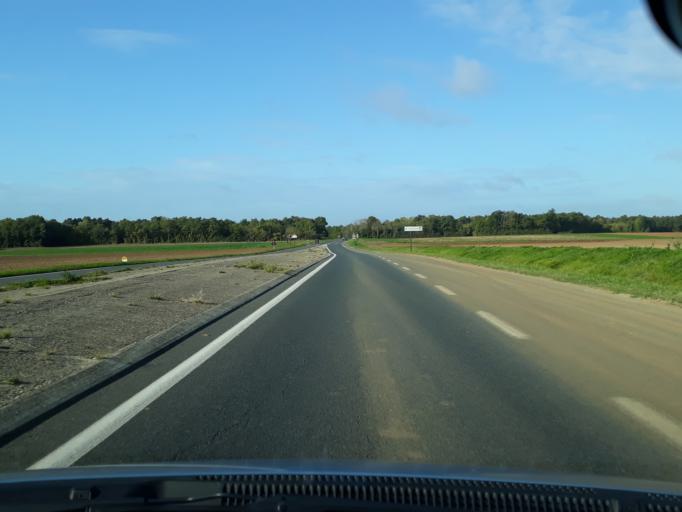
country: FR
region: Ile-de-France
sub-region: Departement de Seine-et-Marne
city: La Chapelle-la-Reine
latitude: 48.3075
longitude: 2.5243
